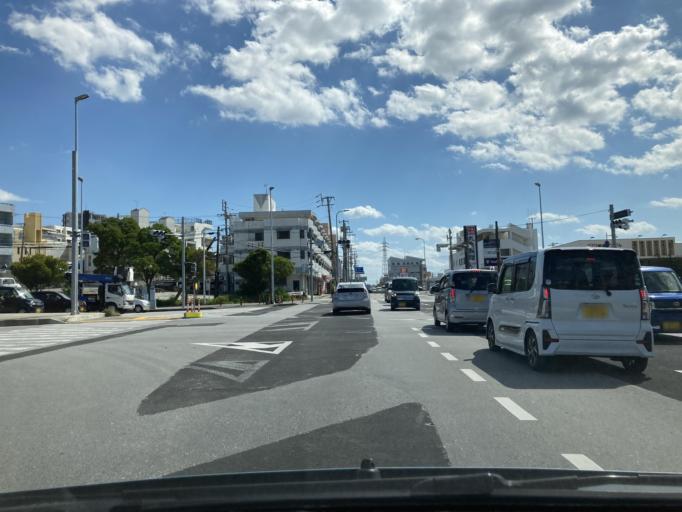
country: JP
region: Okinawa
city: Tomigusuku
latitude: 26.1928
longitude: 127.7069
